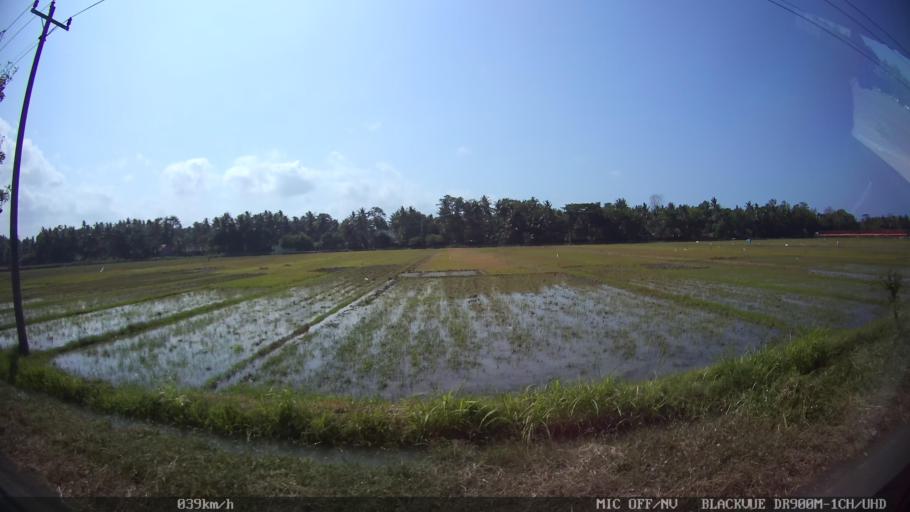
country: ID
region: Daerah Istimewa Yogyakarta
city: Srandakan
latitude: -7.9554
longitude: 110.2173
